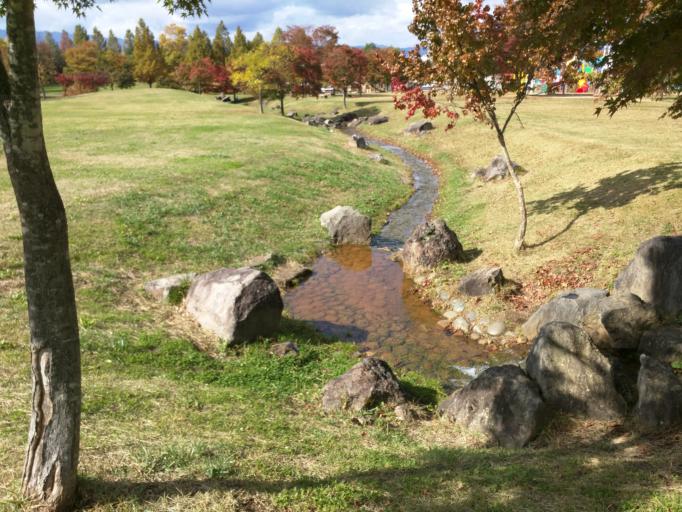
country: JP
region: Fukushima
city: Kitakata
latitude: 37.4599
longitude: 139.9305
